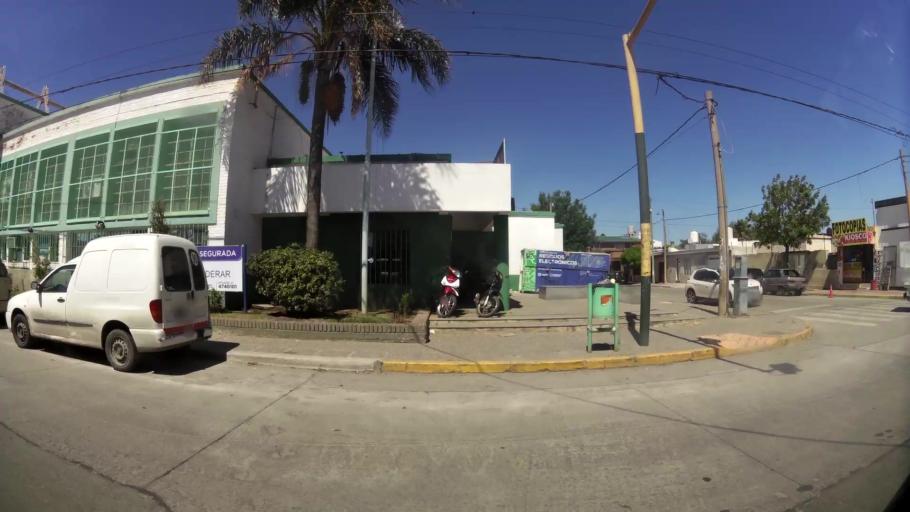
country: AR
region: Cordoba
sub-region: Departamento de Capital
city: Cordoba
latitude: -31.3766
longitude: -64.1478
